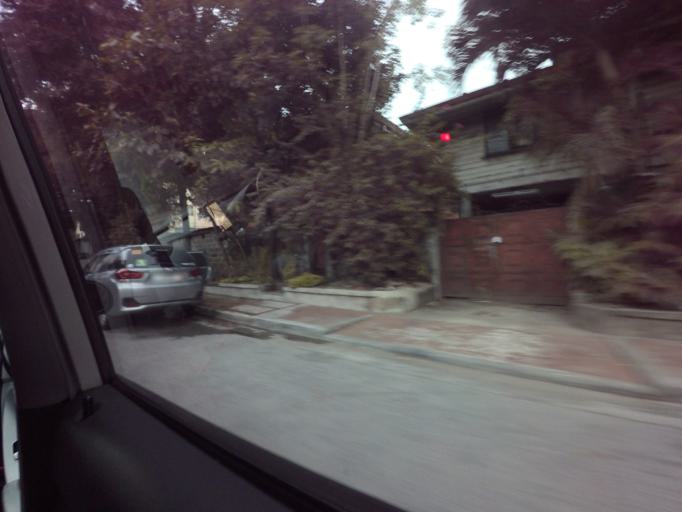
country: PH
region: Metro Manila
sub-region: City of Manila
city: Manila
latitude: 14.6169
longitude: 121.0044
